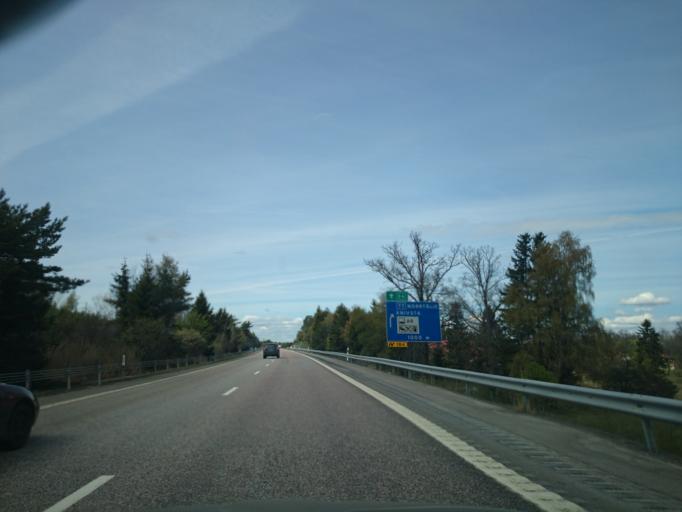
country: SE
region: Uppsala
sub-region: Knivsta Kommun
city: Knivsta
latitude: 59.7295
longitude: 17.8325
